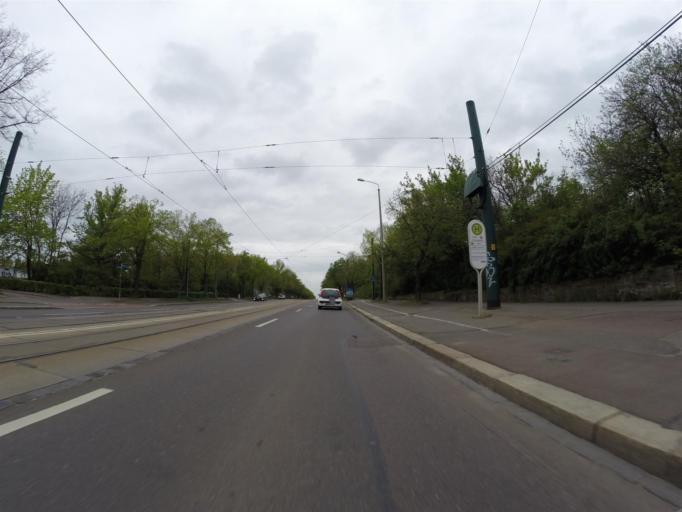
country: DE
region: Saxony-Anhalt
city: Schkopau
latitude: 51.4477
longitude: 11.9840
